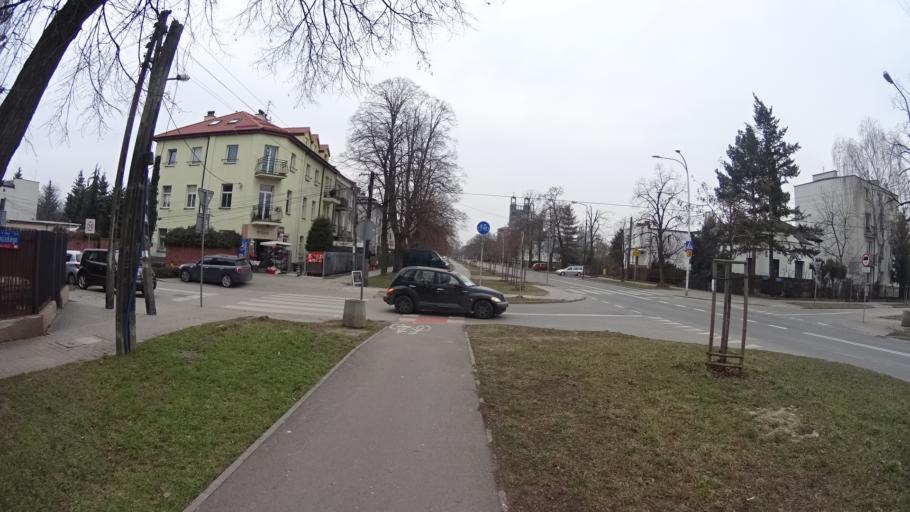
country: PL
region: Masovian Voivodeship
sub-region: Warszawa
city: Ursus
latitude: 52.2083
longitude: 20.9008
